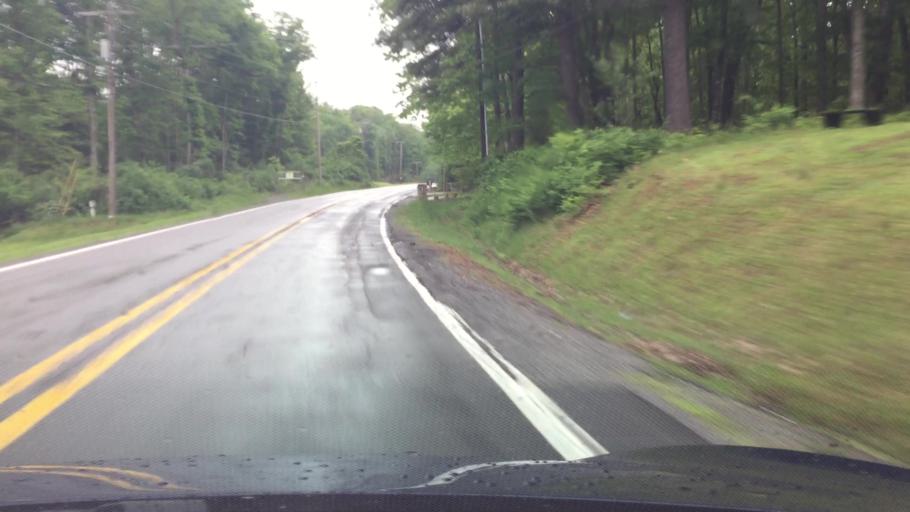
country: US
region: West Virginia
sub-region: Raleigh County
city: Shady Spring
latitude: 37.6904
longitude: -81.0623
